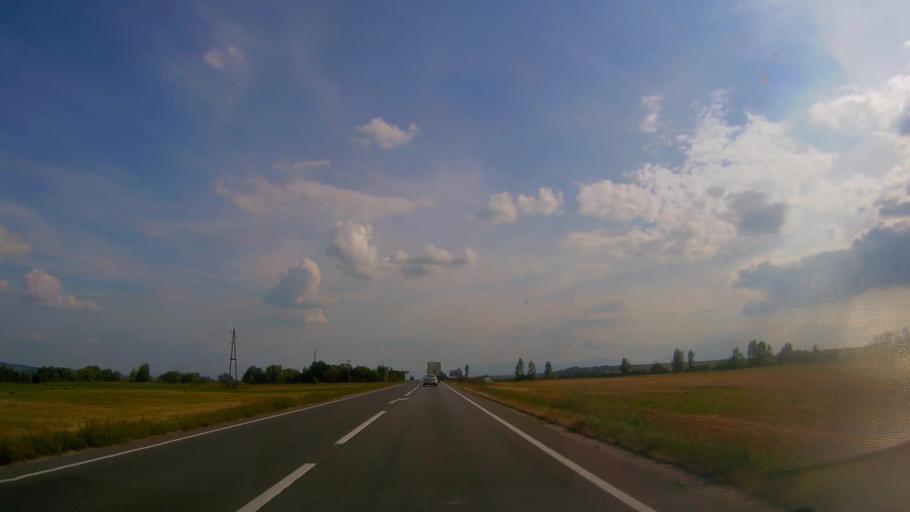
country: RO
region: Brasov
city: Maierus
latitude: 45.8721
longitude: 25.5417
